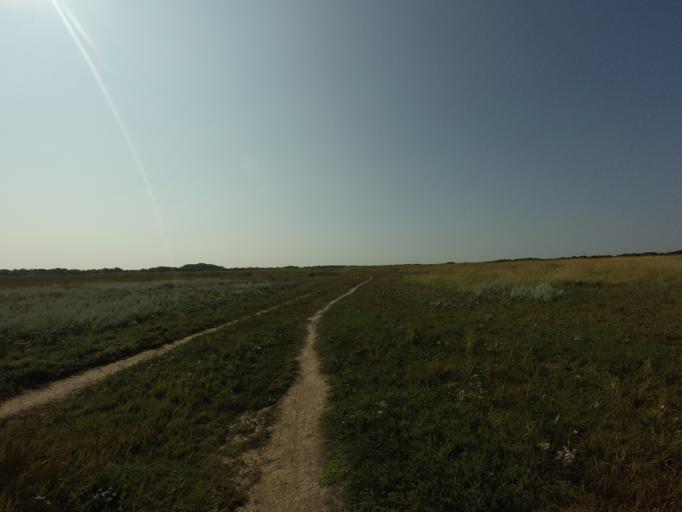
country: NL
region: Friesland
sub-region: Gemeente Schiermonnikoog
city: Schiermonnikoog
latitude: 53.4898
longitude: 6.2303
